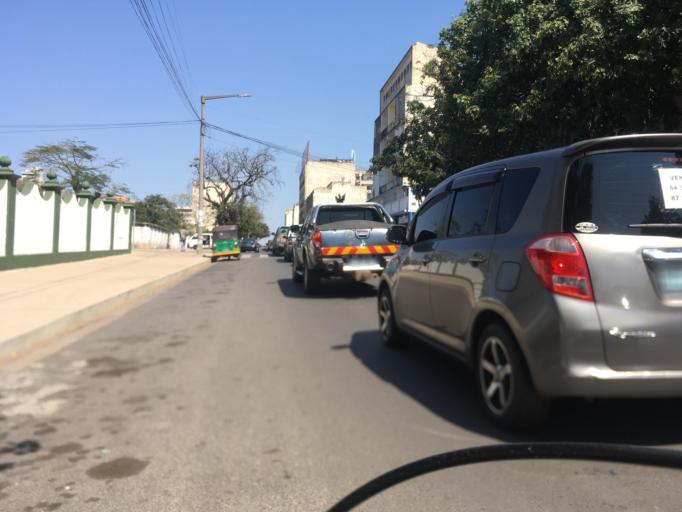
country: MZ
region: Maputo City
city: Maputo
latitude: -25.9608
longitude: 32.5748
